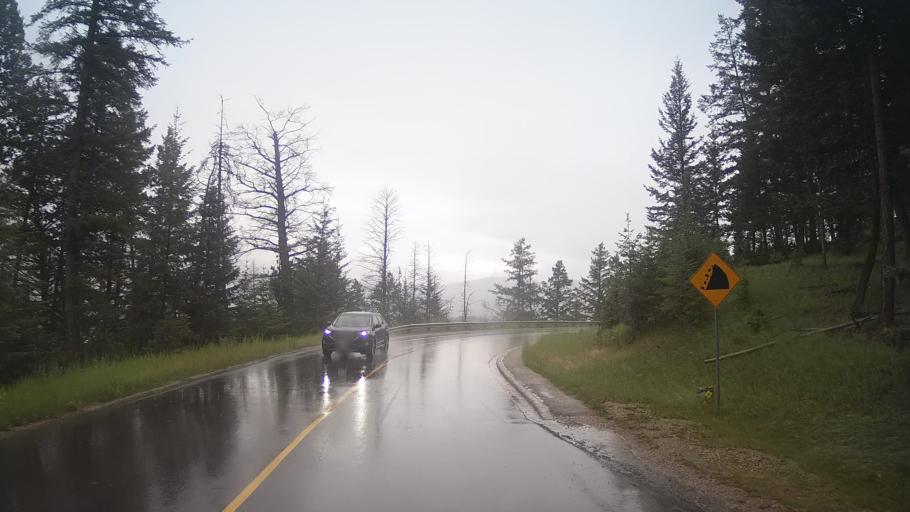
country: CA
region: Alberta
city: Jasper Park Lodge
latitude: 52.8894
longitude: -118.0812
